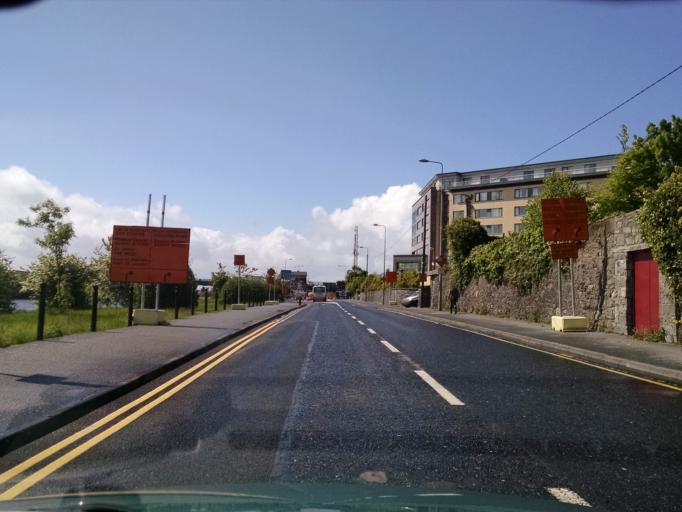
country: IE
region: Connaught
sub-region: County Galway
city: Gaillimh
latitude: 53.2749
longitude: -9.0415
